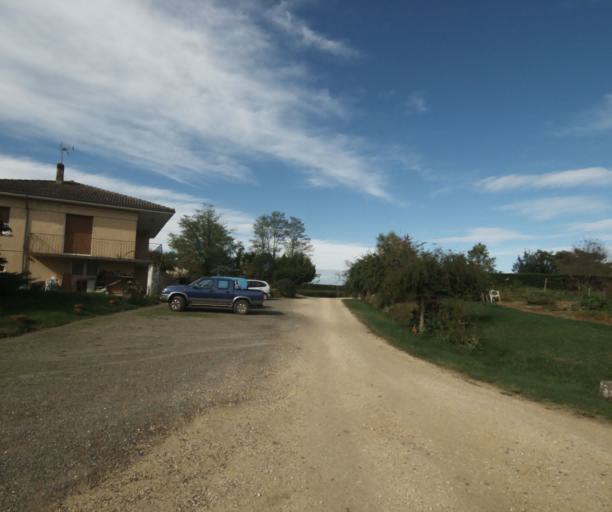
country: FR
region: Midi-Pyrenees
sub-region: Departement du Gers
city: Cazaubon
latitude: 43.9028
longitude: -0.1493
